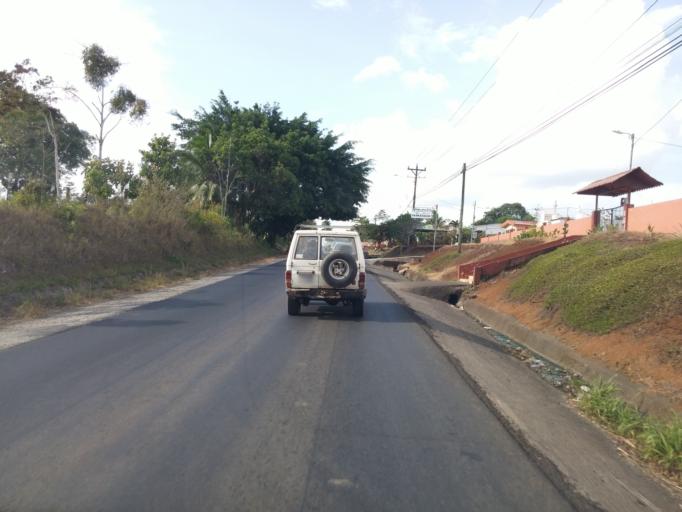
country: CR
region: Alajuela
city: Quesada
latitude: 10.4227
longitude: -84.4680
